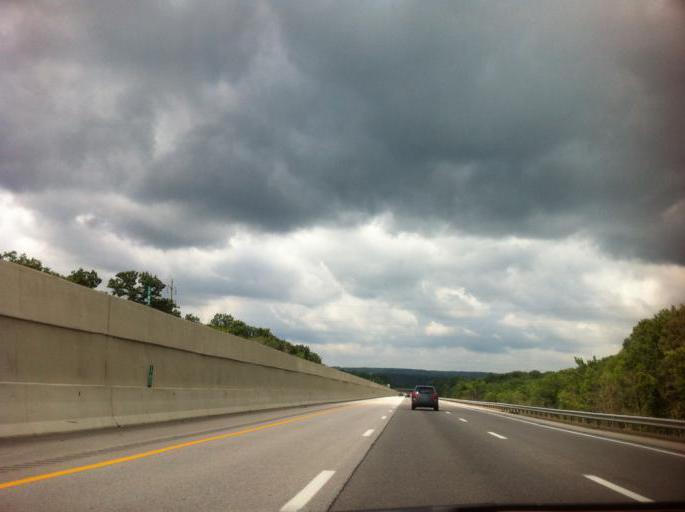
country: US
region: Ohio
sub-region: Summit County
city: Boston Heights
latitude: 41.2576
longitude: -81.5250
